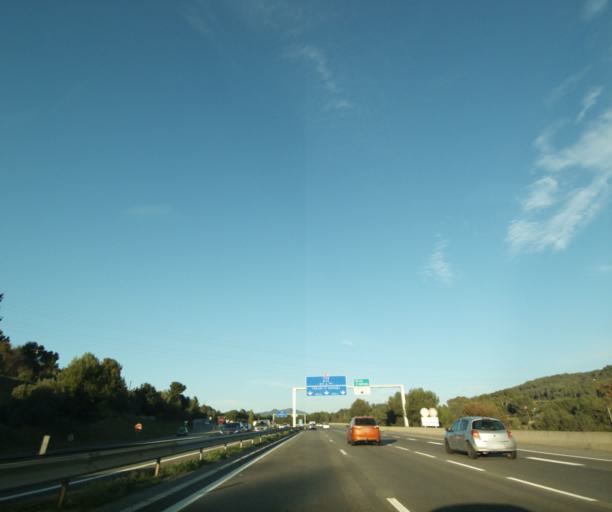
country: FR
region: Provence-Alpes-Cote d'Azur
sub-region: Departement des Bouches-du-Rhone
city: Roquevaire
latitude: 43.3491
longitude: 5.6183
